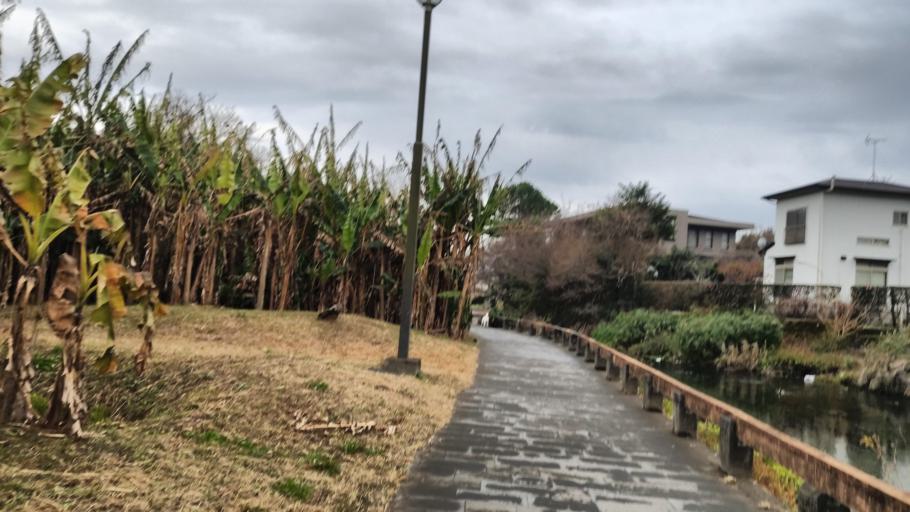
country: JP
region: Kumamoto
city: Kumamoto
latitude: 32.7853
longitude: 130.7343
